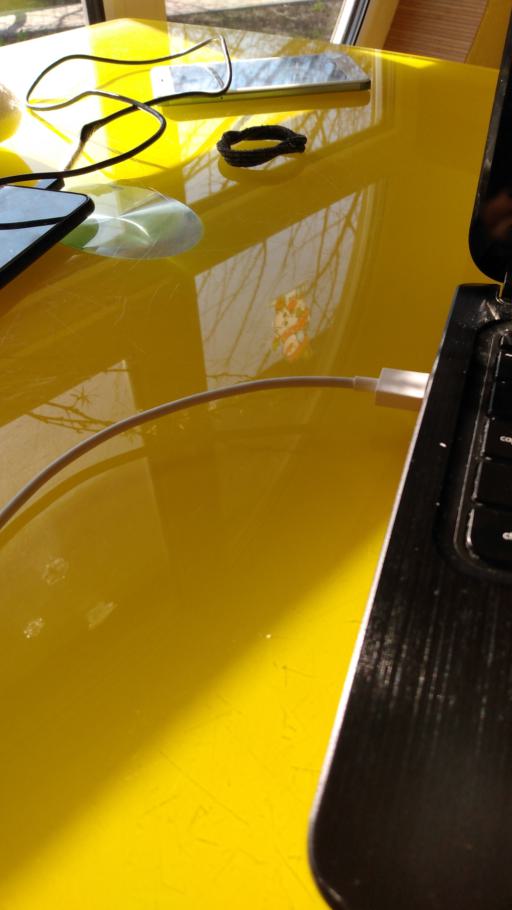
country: RU
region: Novgorod
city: Malaya Vishera
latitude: 58.4988
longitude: 32.2431
